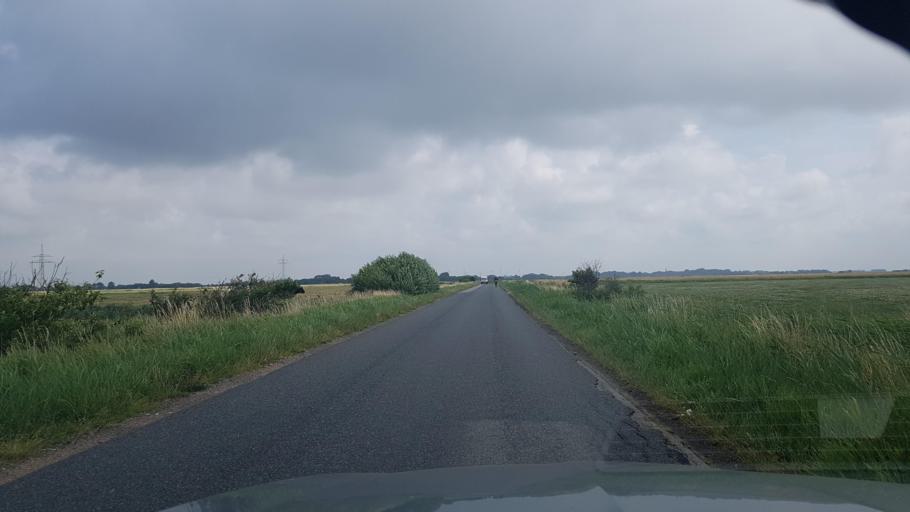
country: DE
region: Schleswig-Holstein
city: Sankt Peter-Ording
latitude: 54.3115
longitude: 8.6599
